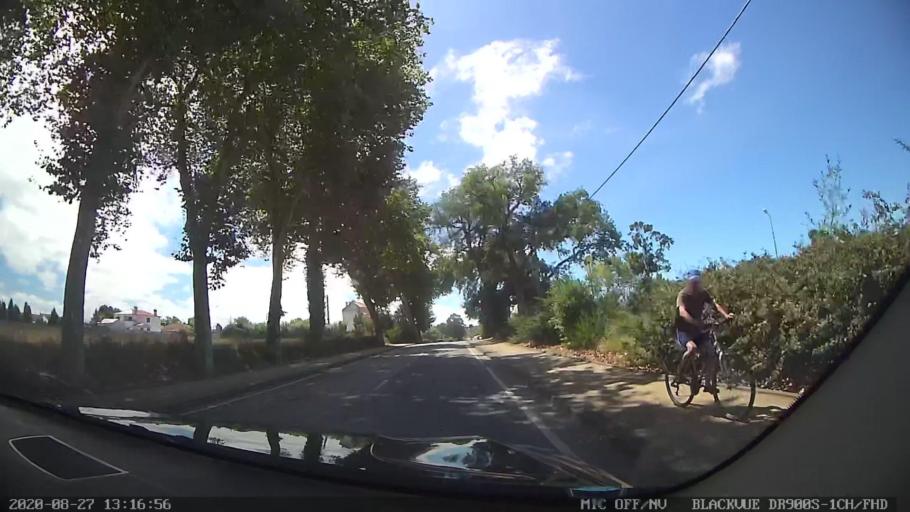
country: PT
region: Aveiro
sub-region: Ilhavo
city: Ilhavo
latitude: 40.5851
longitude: -8.6794
